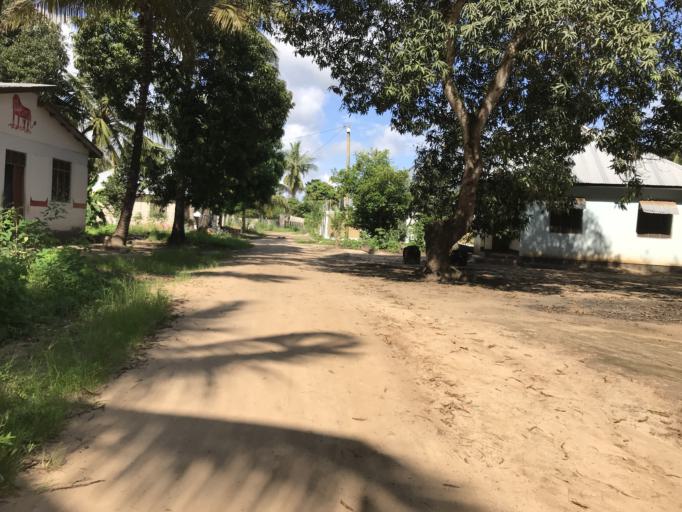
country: TZ
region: Dar es Salaam
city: Dar es Salaam
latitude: -6.8894
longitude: 39.4339
